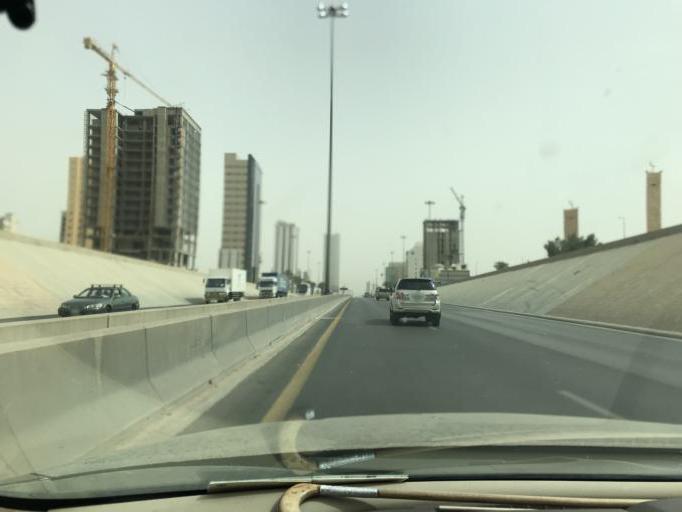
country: SA
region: Ar Riyad
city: Riyadh
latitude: 24.8092
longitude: 46.6226
